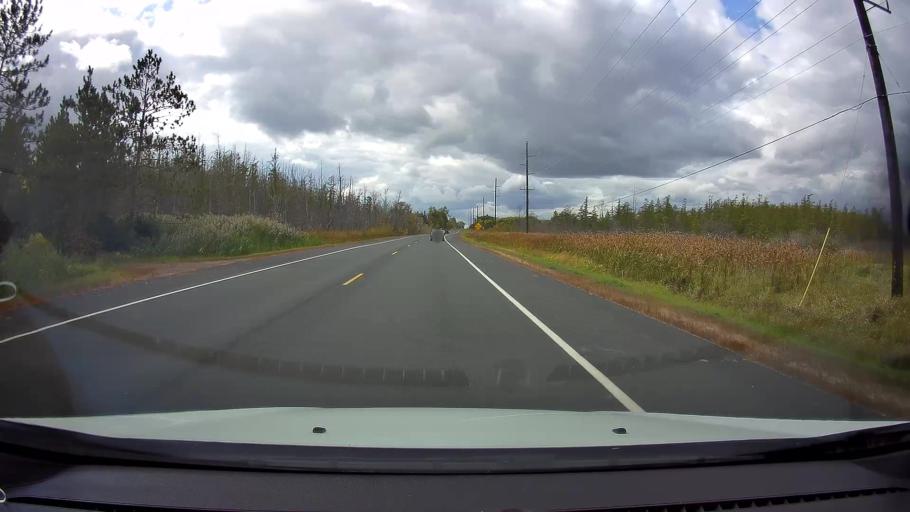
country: US
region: Minnesota
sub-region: Chisago County
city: Shafer
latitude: 45.3973
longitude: -92.7198
